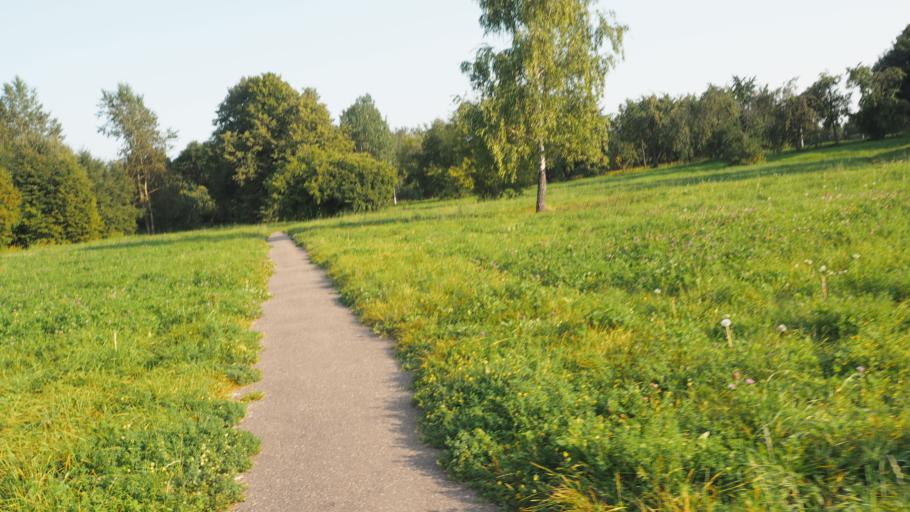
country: RU
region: Moscow
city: Orekhovo-Borisovo Severnoye
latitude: 55.6213
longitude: 37.6870
